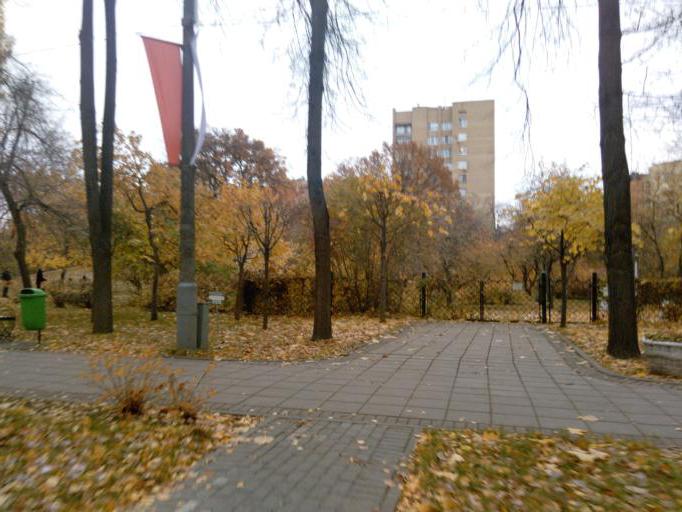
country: RU
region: Moskovskaya
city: Dorogomilovo
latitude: 55.7292
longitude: 37.5775
